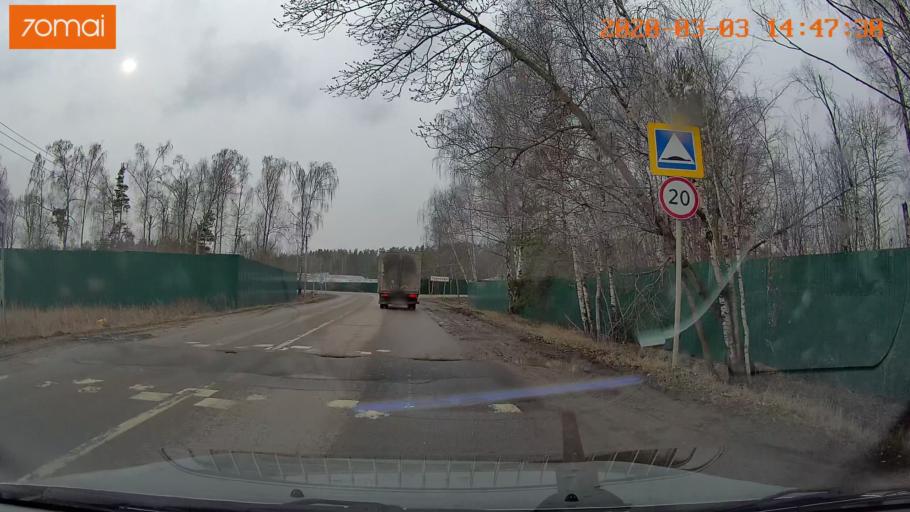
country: RU
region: Moskovskaya
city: Korenevo
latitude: 55.6919
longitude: 38.0468
